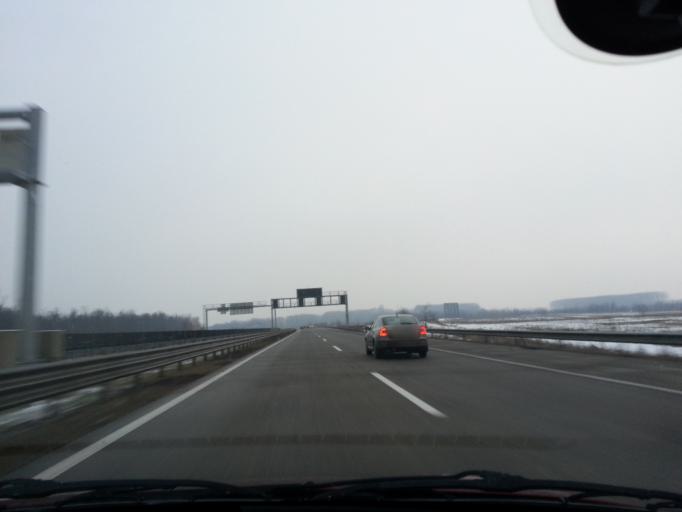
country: HU
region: Pest
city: Ecser
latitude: 47.4269
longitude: 19.3228
